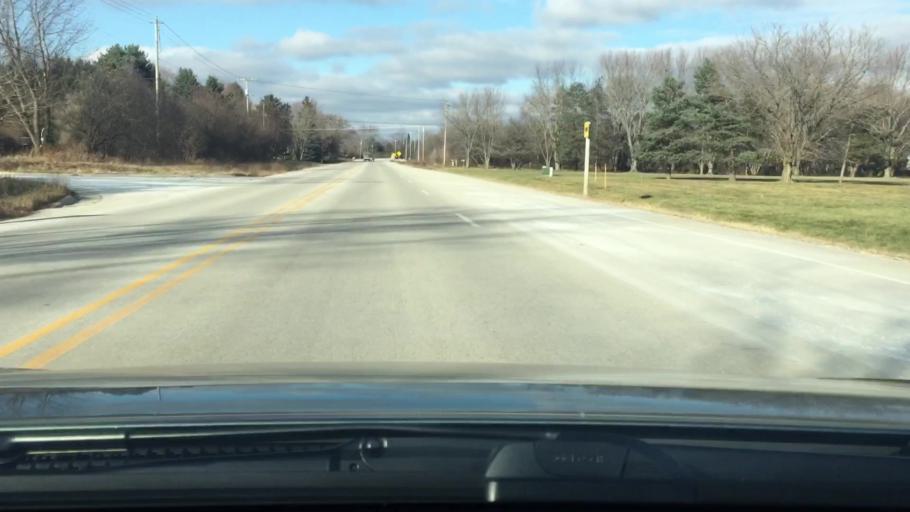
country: US
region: Wisconsin
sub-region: Waukesha County
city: Wales
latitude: 42.9795
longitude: -88.3780
